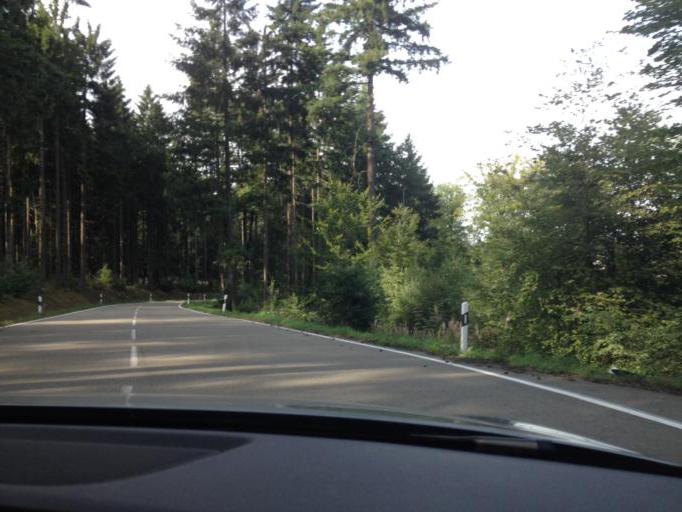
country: DE
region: Rheinland-Pfalz
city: Dunzweiler
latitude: 49.4058
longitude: 7.2982
